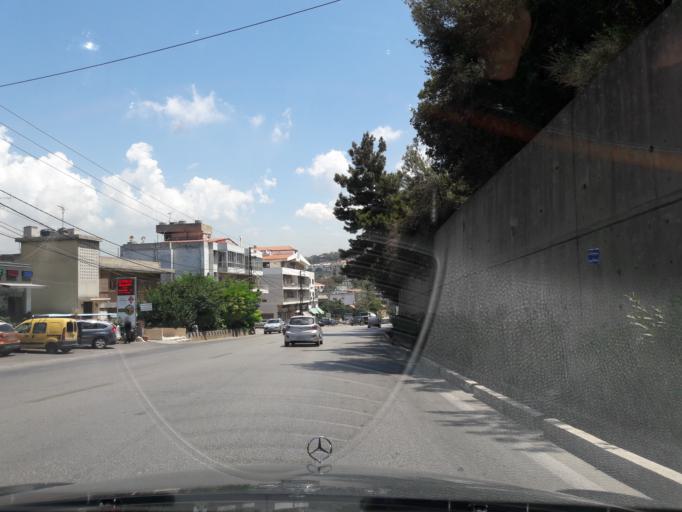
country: LB
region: Mont-Liban
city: Djounie
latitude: 33.9235
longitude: 35.6313
